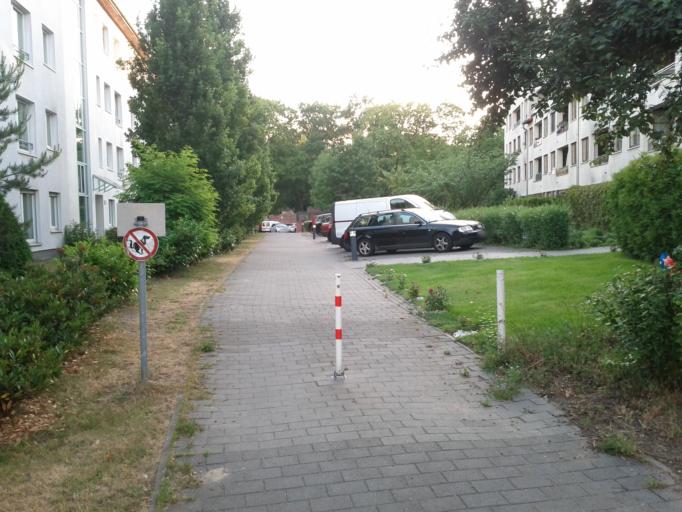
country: DE
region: Berlin
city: Kopenick Bezirk
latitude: 52.4422
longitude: 13.5683
